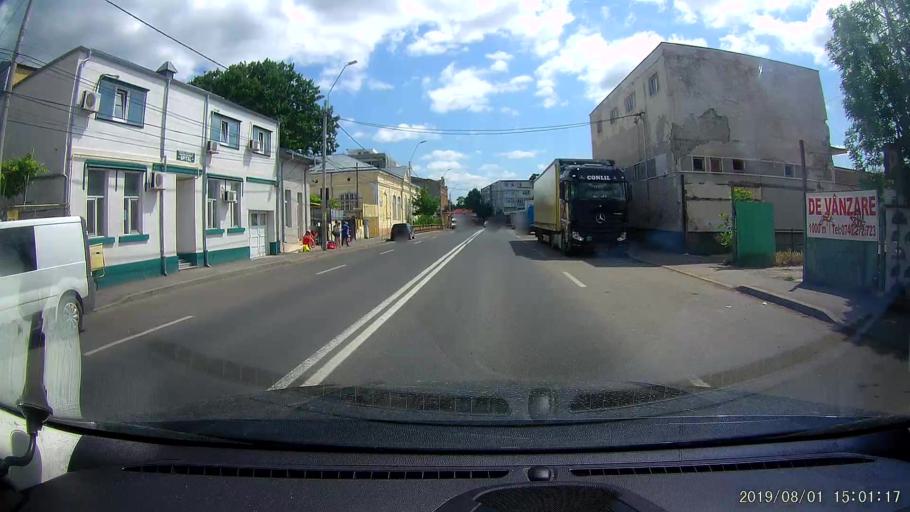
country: RO
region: Braila
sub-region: Municipiul Braila
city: Braila
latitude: 45.2728
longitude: 27.9605
